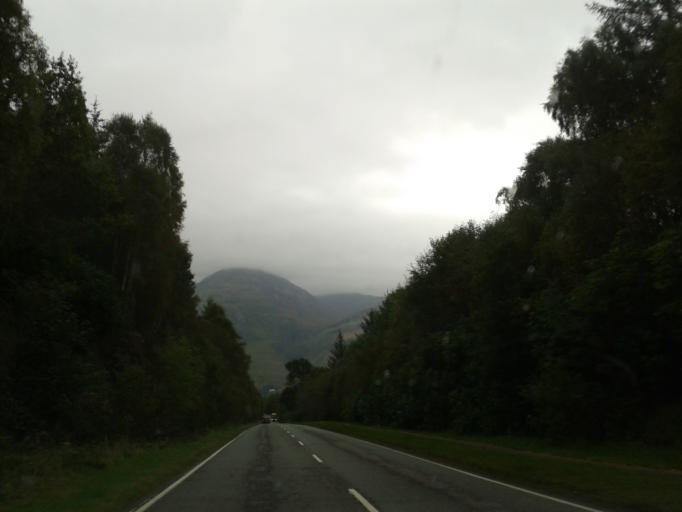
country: GB
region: Scotland
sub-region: Highland
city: Fort William
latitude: 57.2373
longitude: -5.4377
